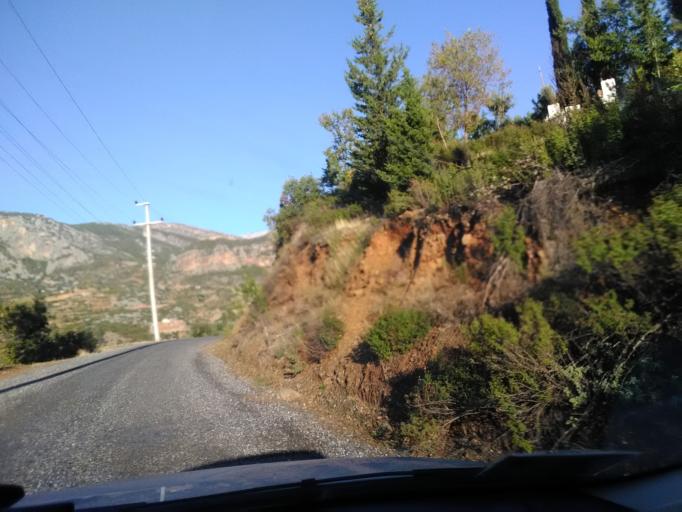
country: TR
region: Antalya
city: Gazipasa
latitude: 36.3172
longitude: 32.4175
